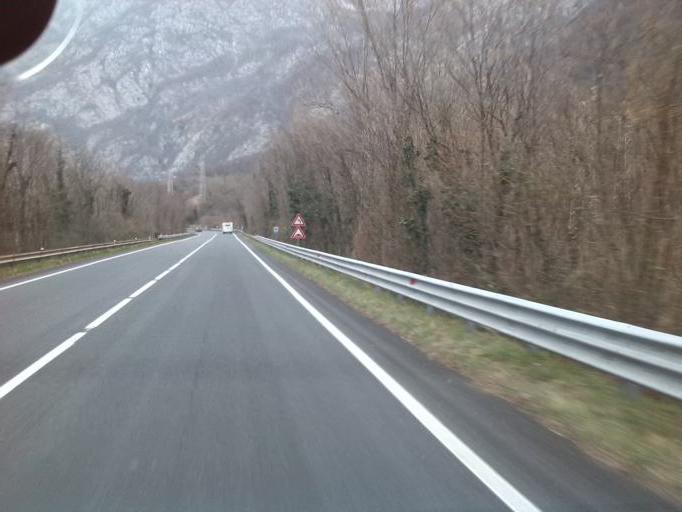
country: IT
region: Friuli Venezia Giulia
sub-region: Provincia di Udine
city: Venzone
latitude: 46.3470
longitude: 13.1415
